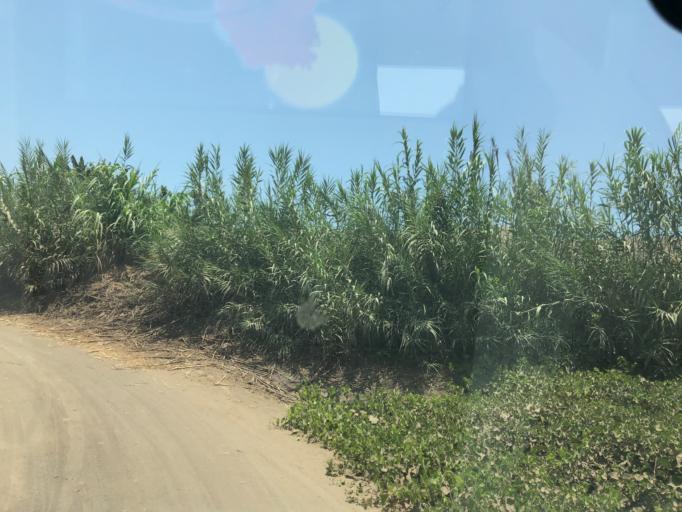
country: PE
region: Lima
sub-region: Provincia de Canete
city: Quilmana
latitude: -12.9974
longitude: -76.4432
